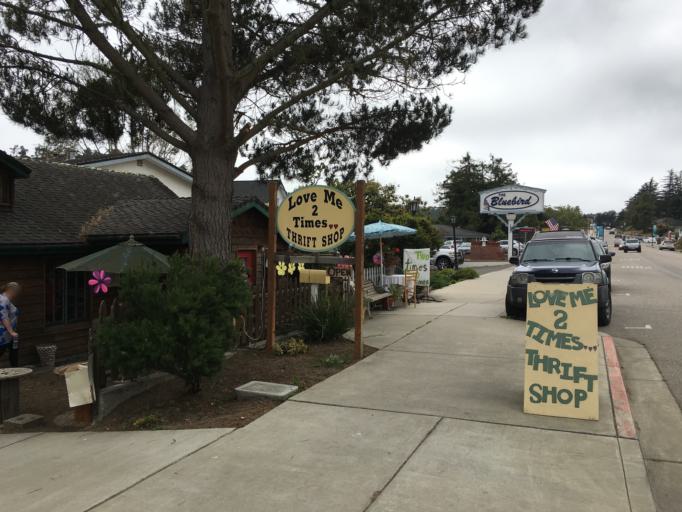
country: US
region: California
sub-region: San Luis Obispo County
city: Cambria
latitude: 35.5634
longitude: -121.0851
